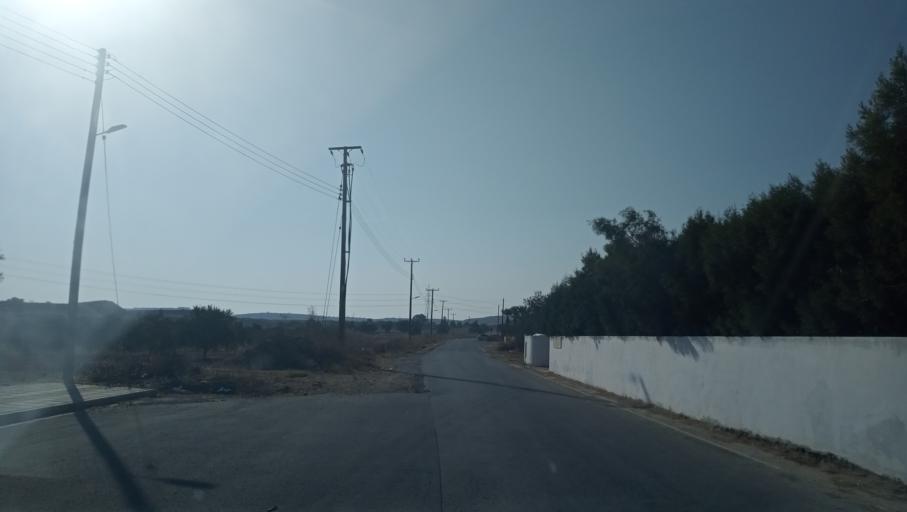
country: CY
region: Lefkosia
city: Geri
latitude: 35.1101
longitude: 33.4301
